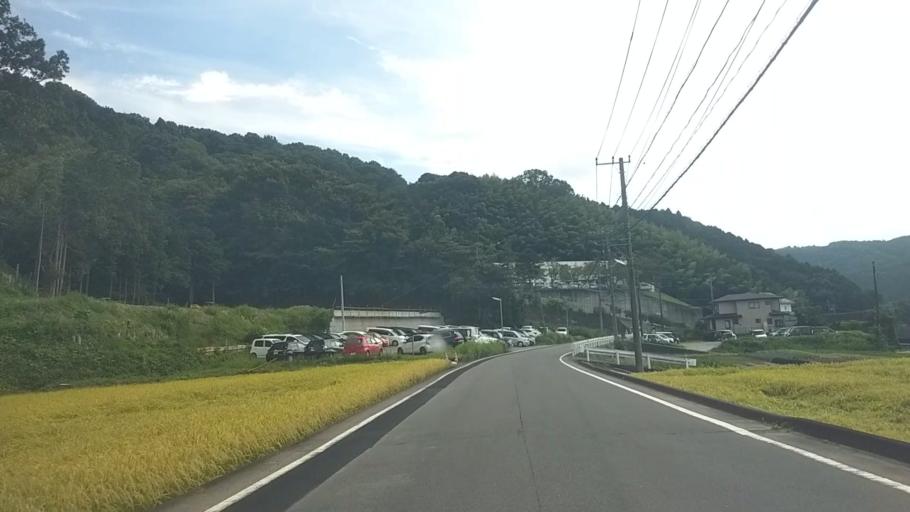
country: JP
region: Shizuoka
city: Ito
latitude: 34.9757
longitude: 138.9768
